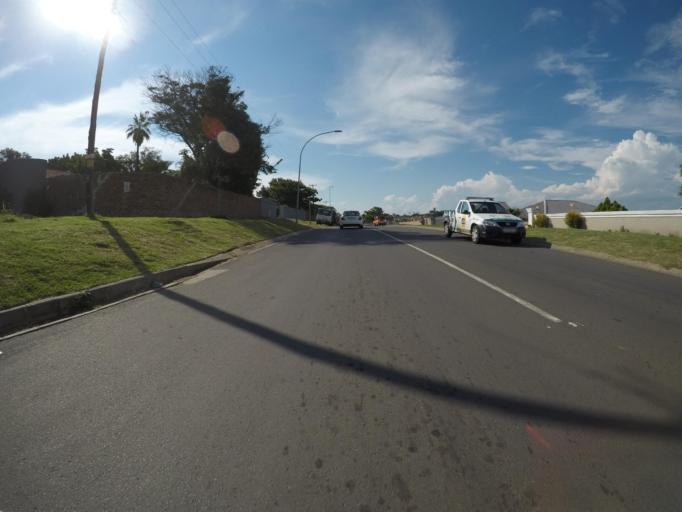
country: ZA
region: Eastern Cape
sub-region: Buffalo City Metropolitan Municipality
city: East London
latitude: -33.0004
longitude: 27.8523
